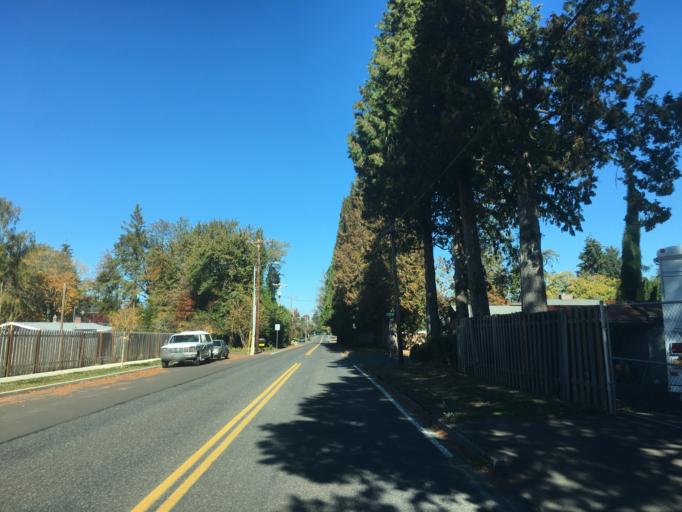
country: US
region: Oregon
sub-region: Multnomah County
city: Gresham
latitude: 45.4816
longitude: -122.4036
